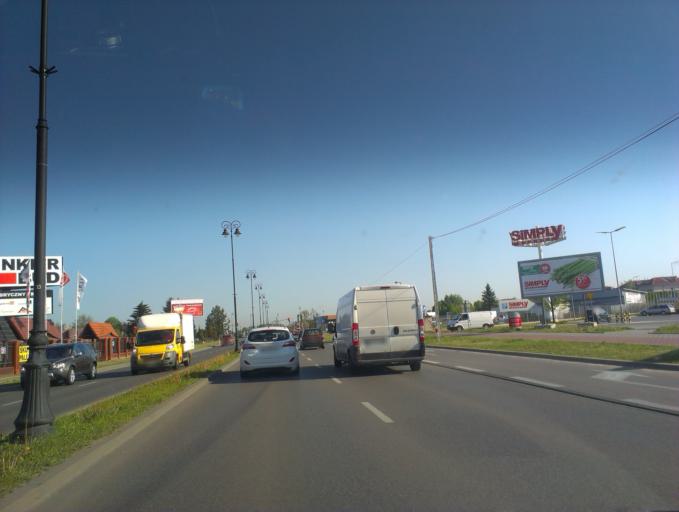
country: PL
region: Masovian Voivodeship
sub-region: Powiat piaseczynski
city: Konstancin-Jeziorna
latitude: 52.1076
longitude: 21.1132
